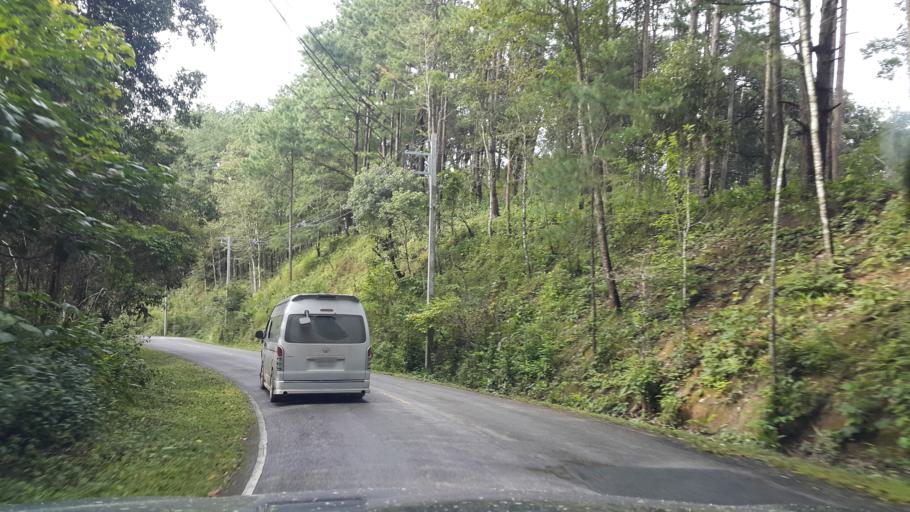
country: TH
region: Chiang Mai
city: Chaem Luang
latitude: 18.9284
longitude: 98.4800
